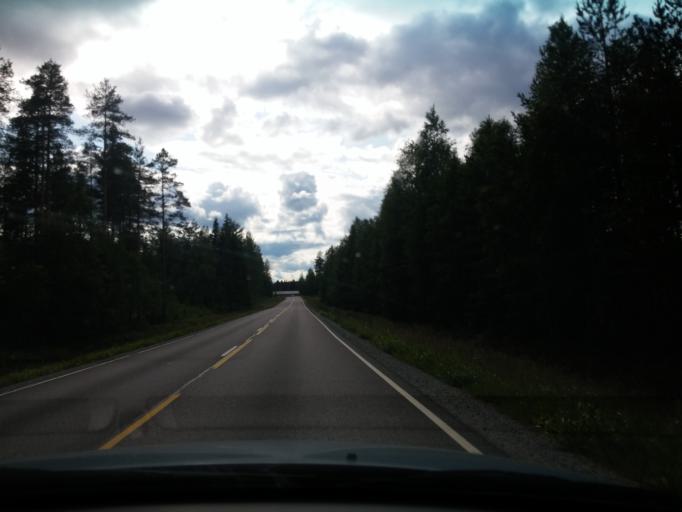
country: FI
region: Central Finland
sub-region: Saarijaervi-Viitasaari
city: Pylkoenmaeki
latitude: 62.6278
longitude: 24.7906
